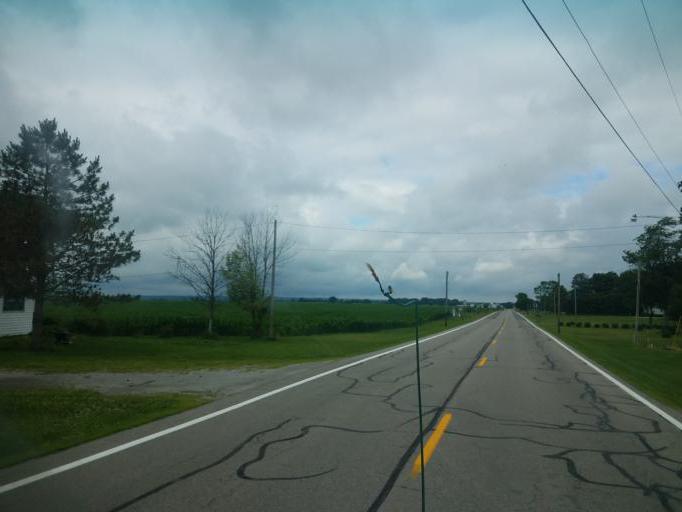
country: US
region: Ohio
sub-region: Champaign County
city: North Lewisburg
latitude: 40.4055
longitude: -83.5504
